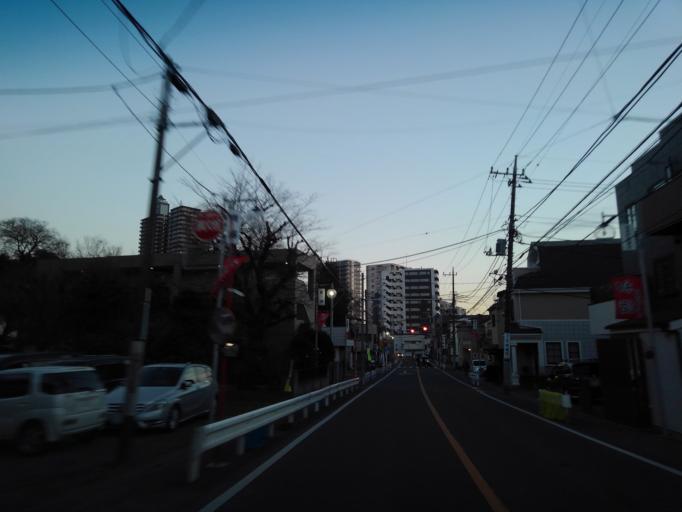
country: JP
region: Saitama
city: Tokorozawa
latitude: 35.7940
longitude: 139.4621
